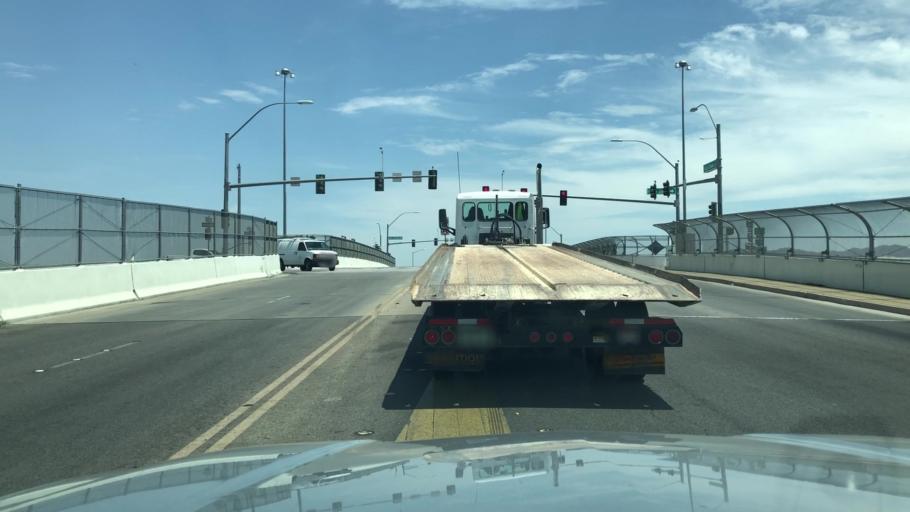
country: US
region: Nevada
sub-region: Clark County
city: Henderson
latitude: 36.0458
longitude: -115.0237
